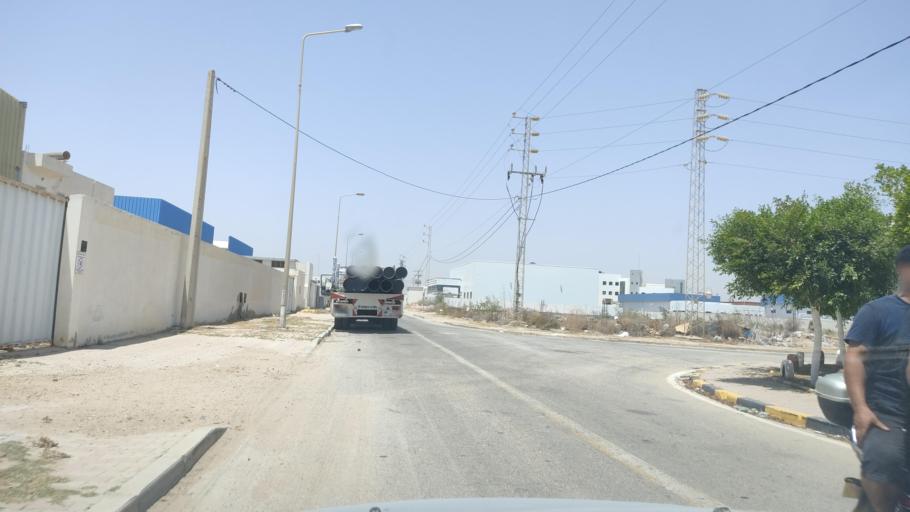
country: TN
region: Safaqis
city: Sfax
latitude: 34.6601
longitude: 10.6965
